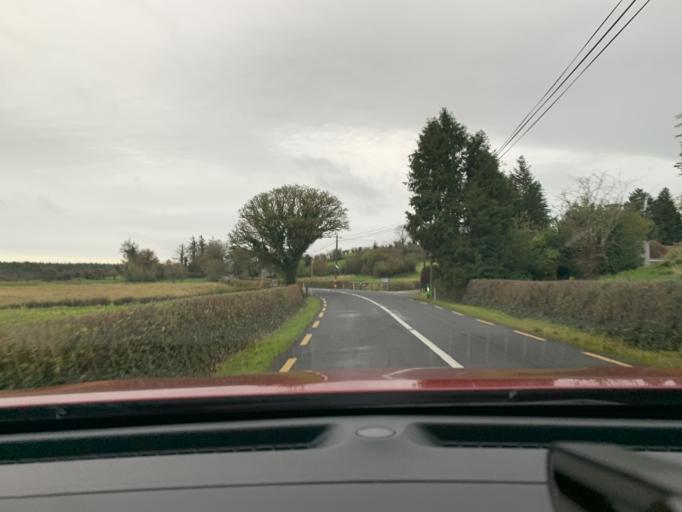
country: IE
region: Connaught
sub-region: Sligo
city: Ballymote
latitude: 54.0484
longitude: -8.5239
